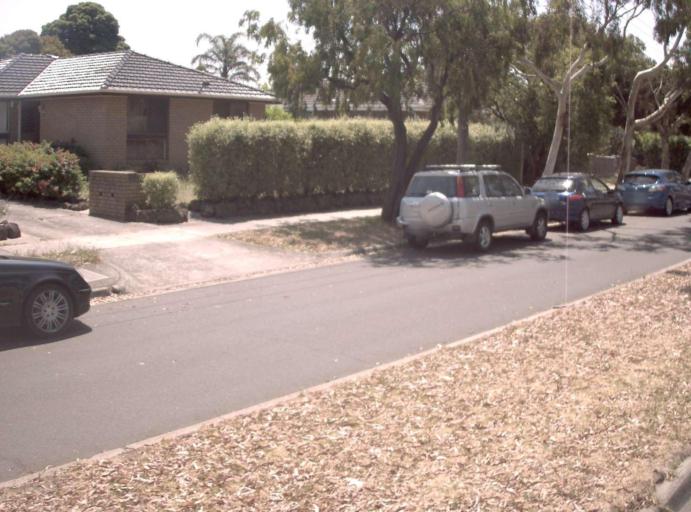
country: AU
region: Victoria
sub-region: Monash
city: Notting Hill
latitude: -37.9000
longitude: 145.1621
